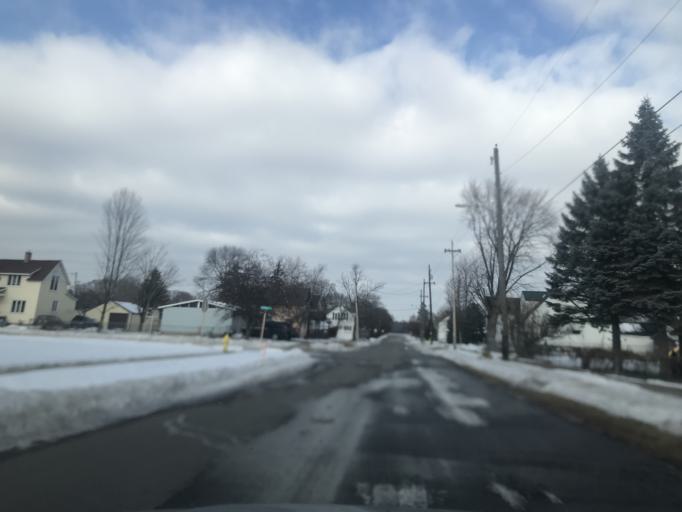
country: US
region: Wisconsin
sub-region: Marinette County
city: Marinette
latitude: 45.1008
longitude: -87.6413
